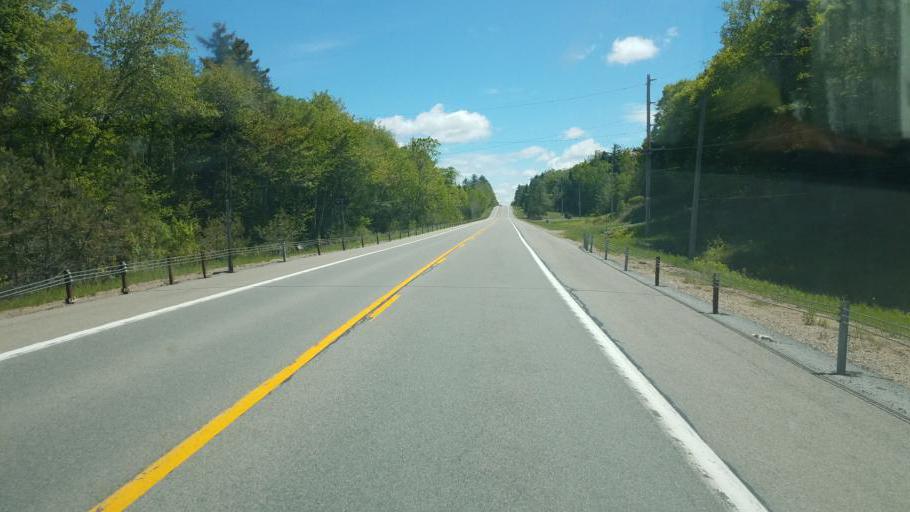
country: US
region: New York
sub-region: Oneida County
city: Boonville
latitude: 43.6796
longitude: -75.0478
